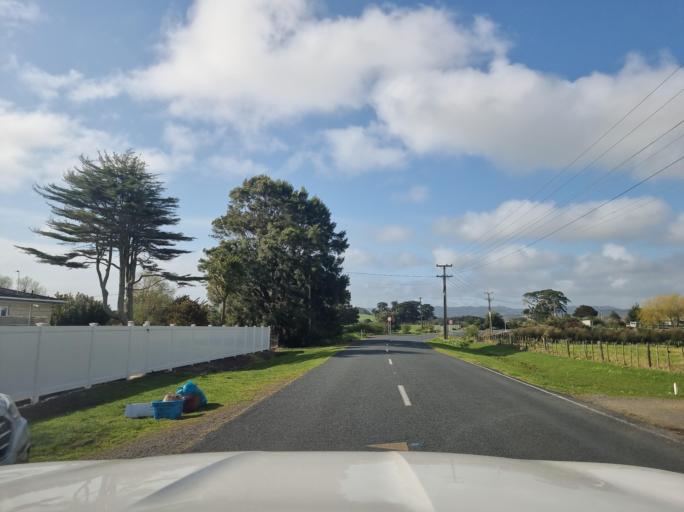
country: NZ
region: Northland
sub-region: Whangarei
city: Ruakaka
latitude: -35.9889
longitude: 174.4499
